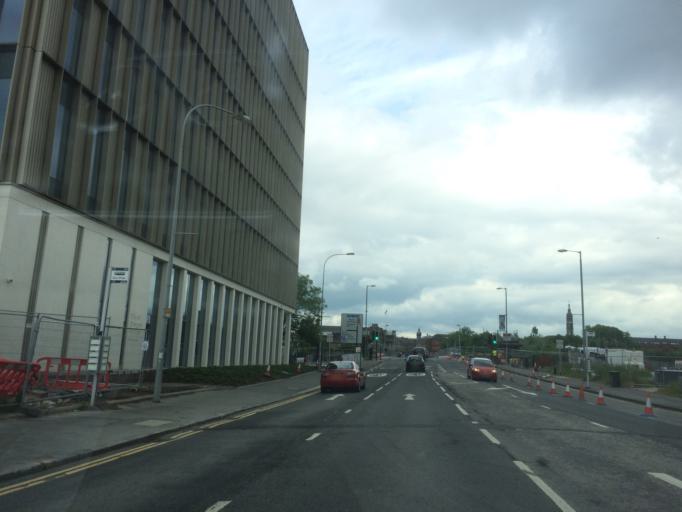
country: GB
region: Scotland
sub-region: Glasgow City
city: Glasgow
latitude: 55.8514
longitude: -4.2484
